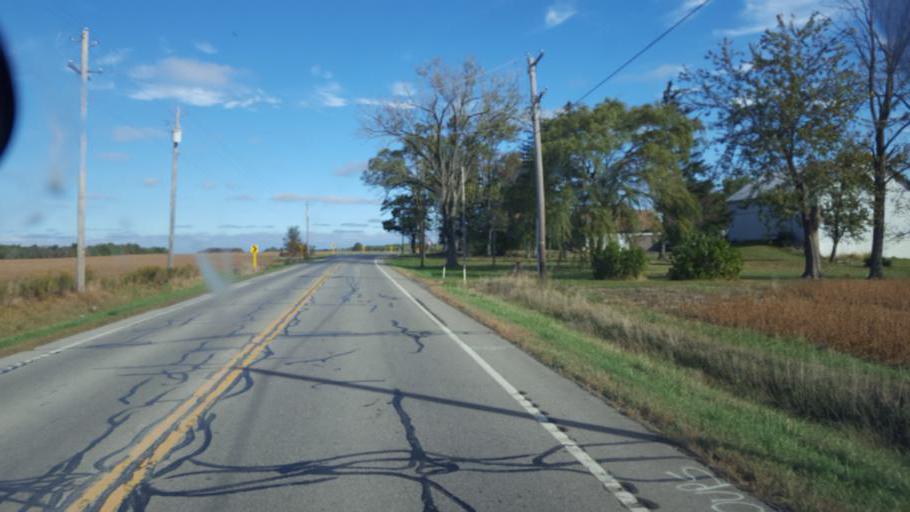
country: US
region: Ohio
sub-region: Huron County
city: Greenwich
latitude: 40.9670
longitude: -82.4955
